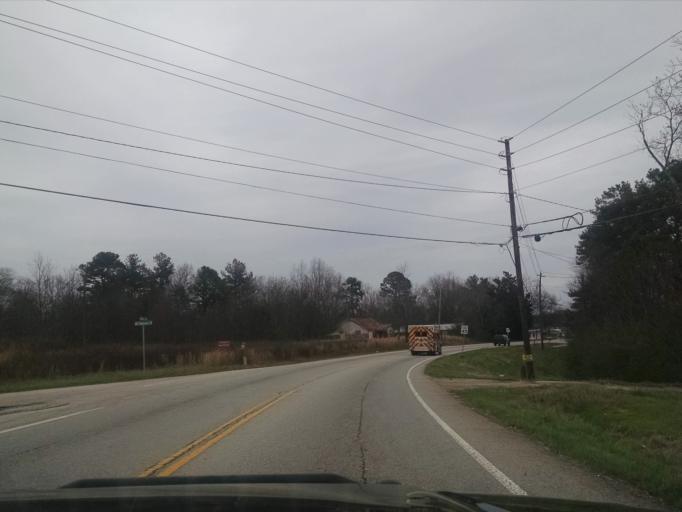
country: US
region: Georgia
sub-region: Hall County
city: Oakwood
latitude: 34.2148
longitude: -83.8778
